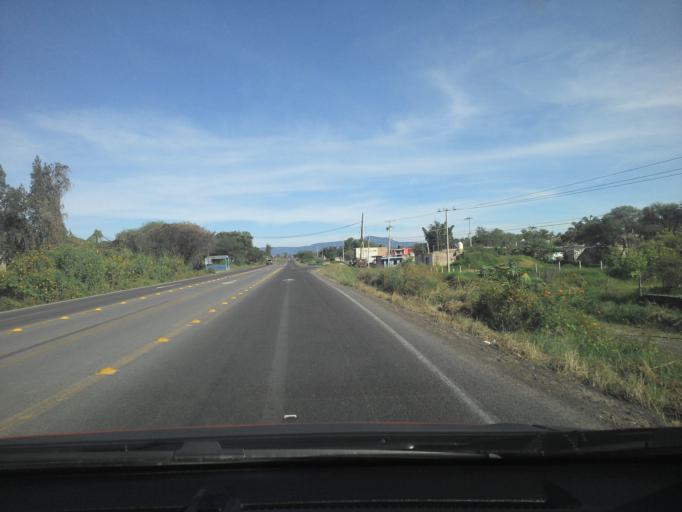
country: MX
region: Jalisco
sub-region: Teuchitlan
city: La Estanzuela
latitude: 20.6737
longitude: -103.8271
